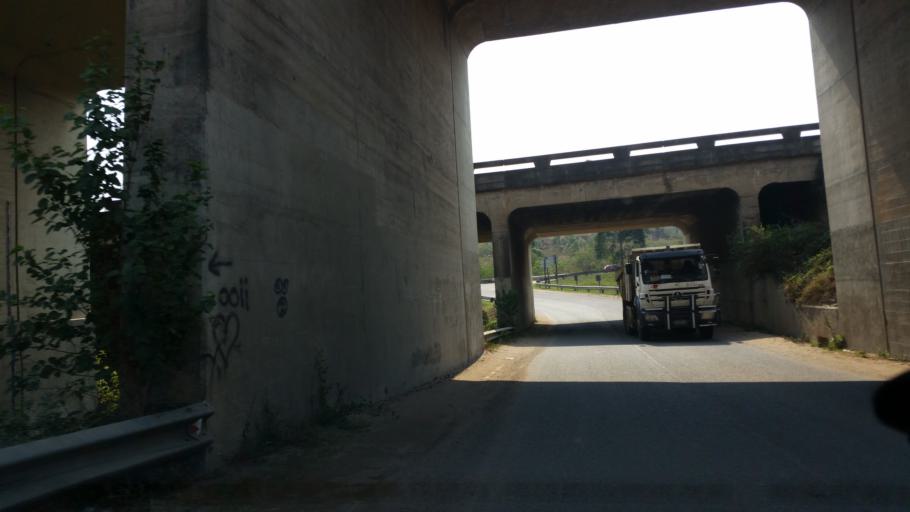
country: ZA
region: KwaZulu-Natal
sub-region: eThekwini Metropolitan Municipality
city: Mpumalanga
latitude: -29.7711
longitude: 30.6842
